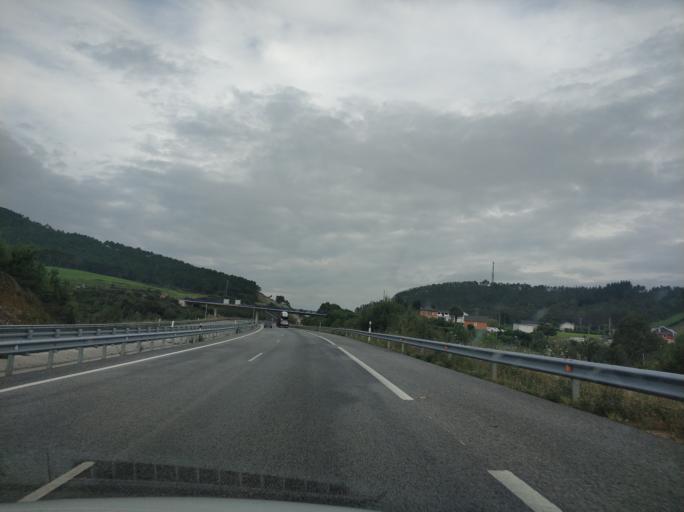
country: ES
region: Asturias
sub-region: Province of Asturias
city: Navia
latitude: 43.5395
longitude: -6.6109
